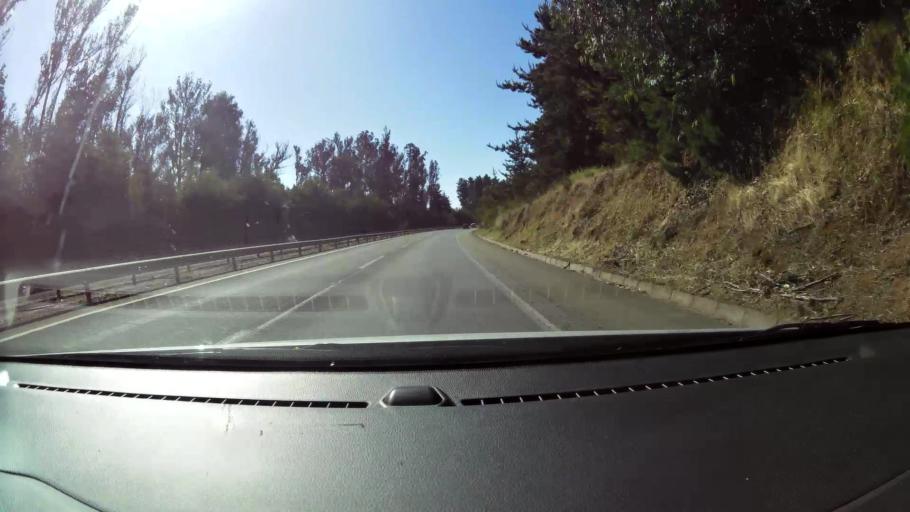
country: CL
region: Valparaiso
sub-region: Provincia de Valparaiso
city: Vina del Mar
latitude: -33.1545
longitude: -71.5549
